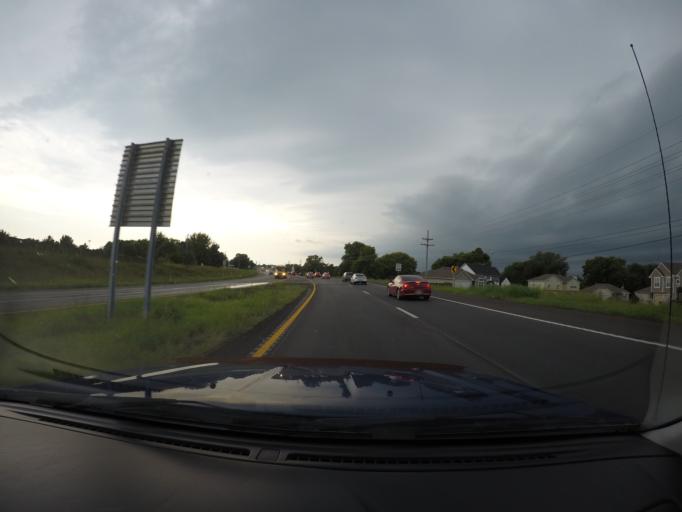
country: US
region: Missouri
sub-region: Jackson County
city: East Independence
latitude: 39.1341
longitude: -94.3461
